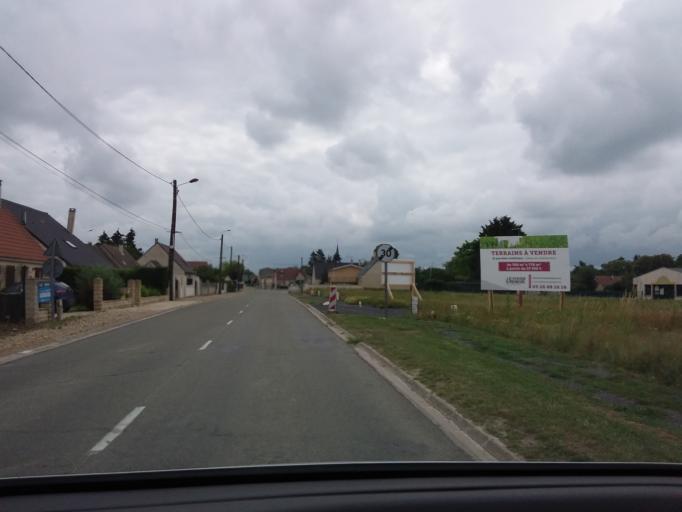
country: FR
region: Champagne-Ardenne
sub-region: Departement de la Marne
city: Cormicy
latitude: 49.4076
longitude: 3.8169
